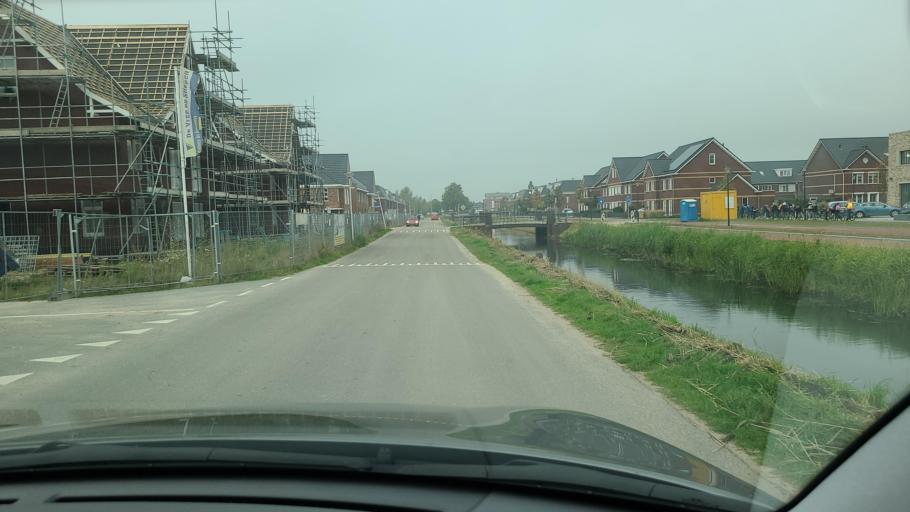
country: NL
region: Gelderland
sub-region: Gemeente Geldermalsen
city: Geldermalsen
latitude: 51.8689
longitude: 5.2931
